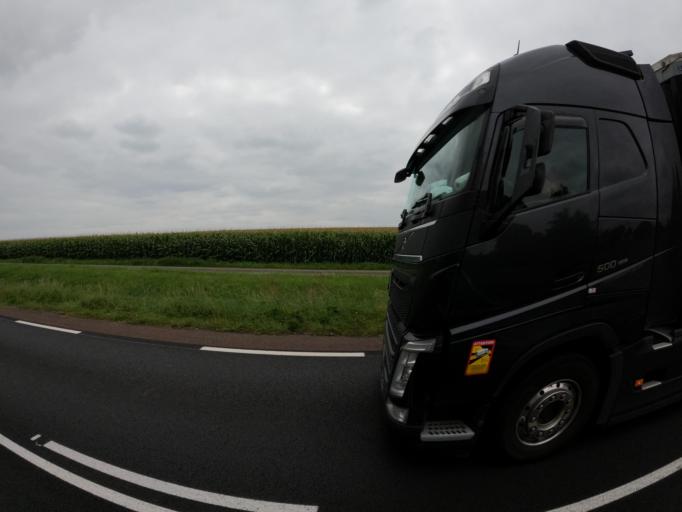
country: FR
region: Pays de la Loire
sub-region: Departement de la Vendee
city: Benet
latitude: 46.3967
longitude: -0.6538
